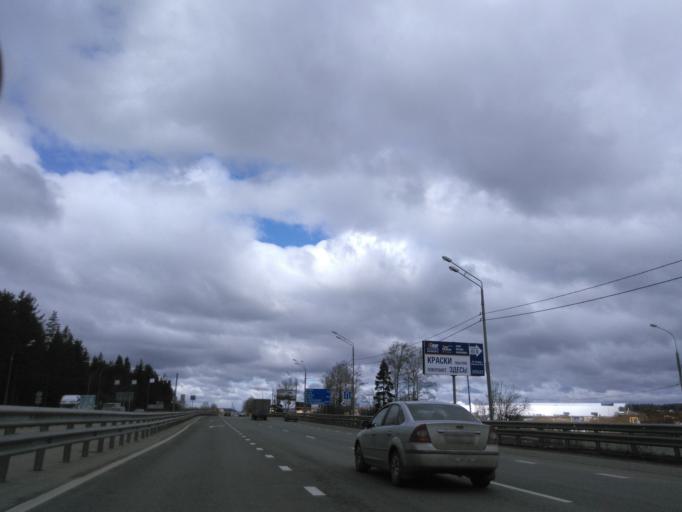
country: RU
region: Moskovskaya
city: Rzhavki
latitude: 55.9908
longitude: 37.2678
